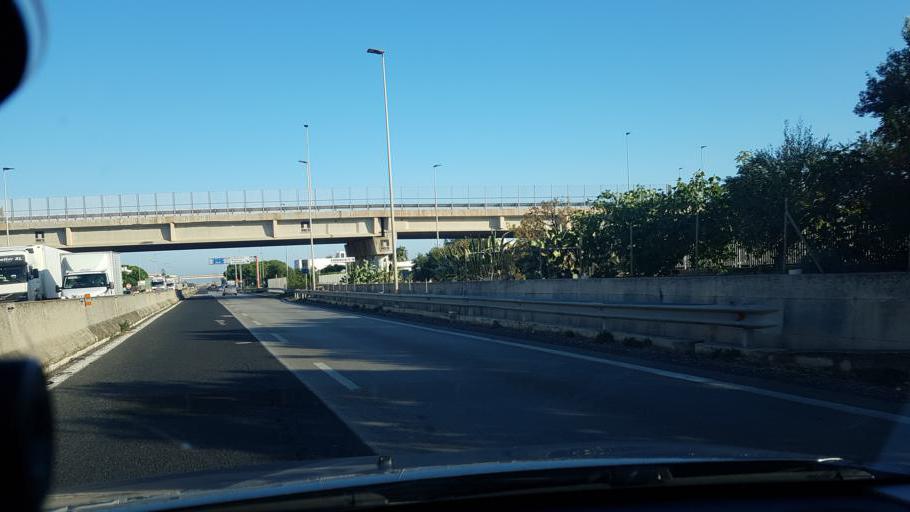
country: IT
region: Apulia
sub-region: Provincia di Brindisi
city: Fasano
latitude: 40.8795
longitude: 17.3387
